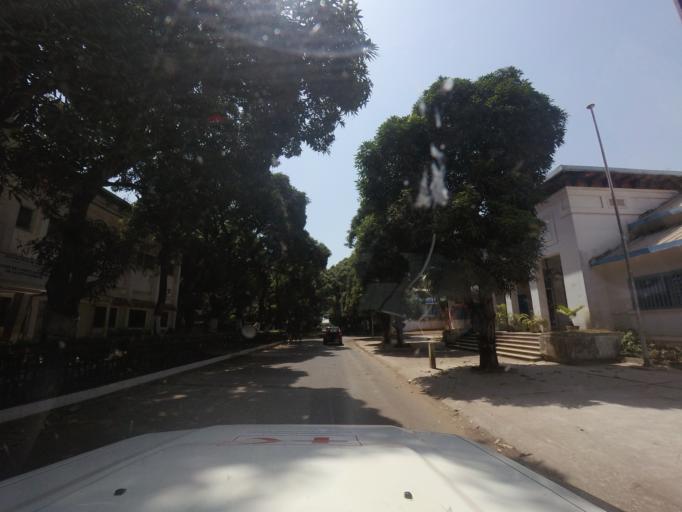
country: GN
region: Conakry
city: Camayenne
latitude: 9.5067
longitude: -13.7176
